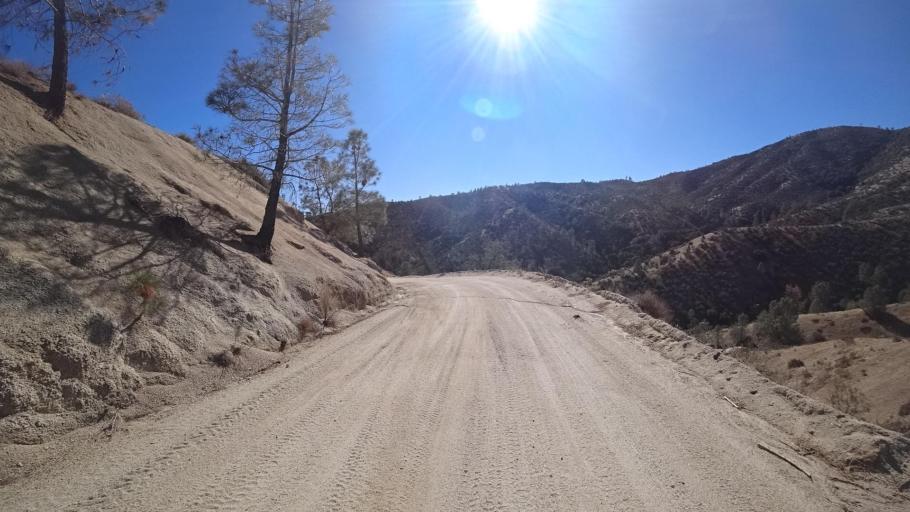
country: US
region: California
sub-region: Kern County
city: Wofford Heights
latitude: 35.6997
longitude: -118.4835
